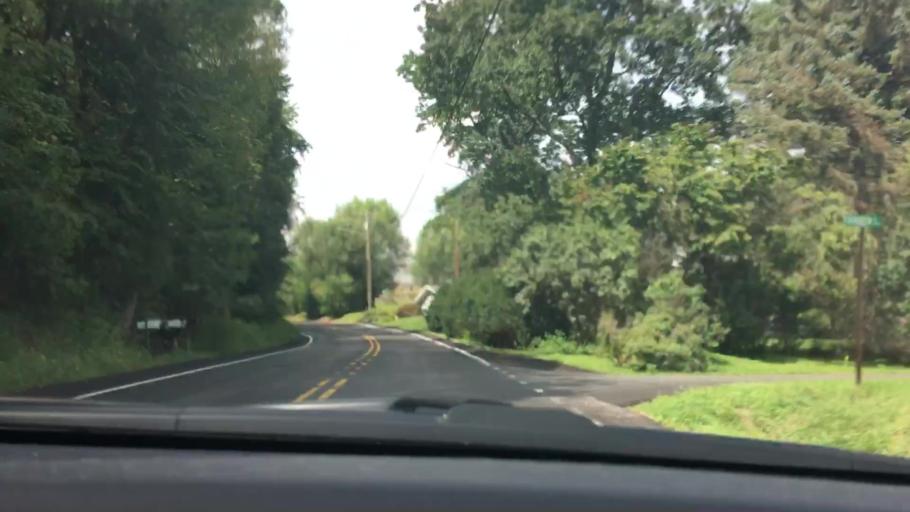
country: US
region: Pennsylvania
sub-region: Allegheny County
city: Versailles
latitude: 40.2930
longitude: -79.8392
